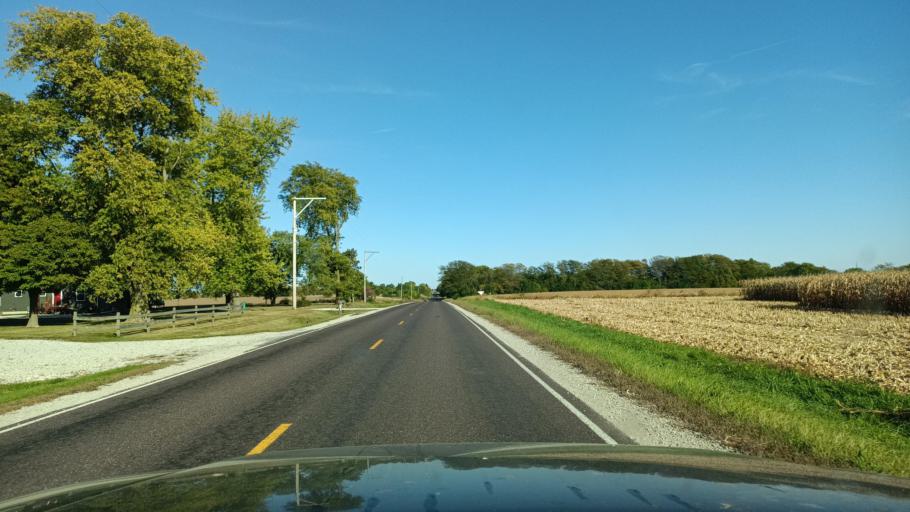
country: US
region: Illinois
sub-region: McLean County
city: Heyworth
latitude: 40.2315
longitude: -89.0110
